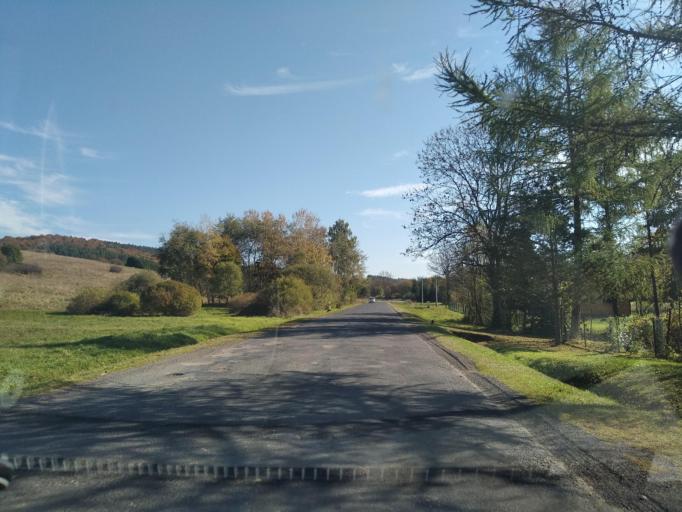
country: PL
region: Subcarpathian Voivodeship
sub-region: Powiat sanocki
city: Bukowsko
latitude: 49.4137
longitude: 21.9753
